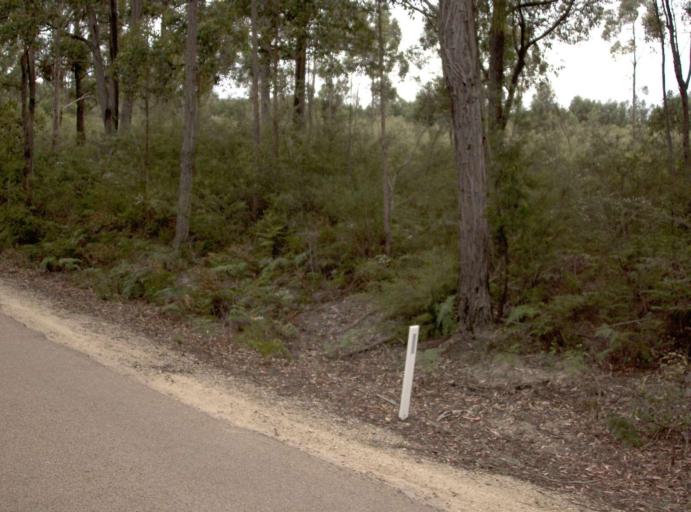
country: AU
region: Victoria
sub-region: East Gippsland
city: Bairnsdale
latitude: -37.7495
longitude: 147.5990
